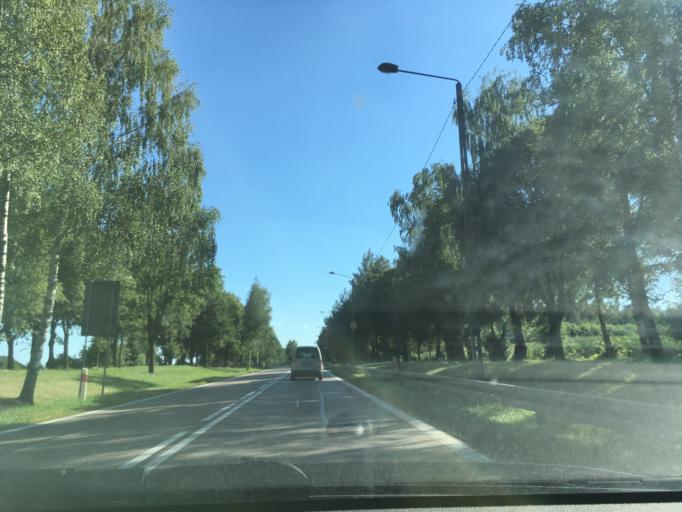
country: PL
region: Podlasie
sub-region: Powiat sokolski
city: Suchowola
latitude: 53.5572
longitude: 23.1008
